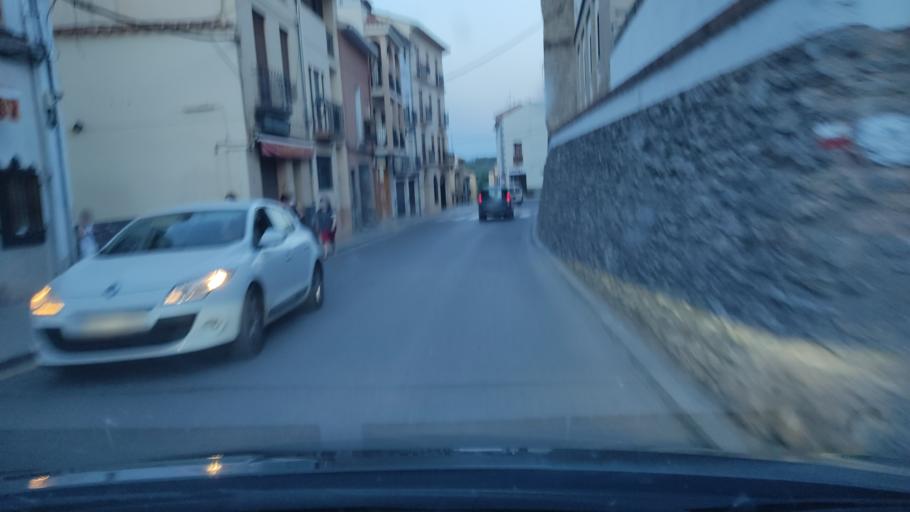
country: ES
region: Valencia
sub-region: Provincia de Castello
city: Jerica
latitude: 39.9125
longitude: -0.5719
